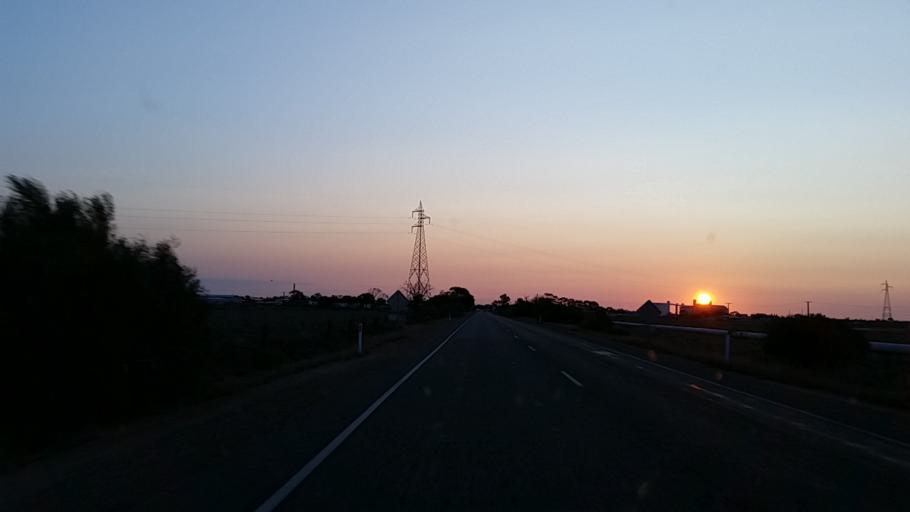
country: AU
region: South Australia
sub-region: Port Pirie City and Dists
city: Solomontown
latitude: -33.1810
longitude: 138.0395
